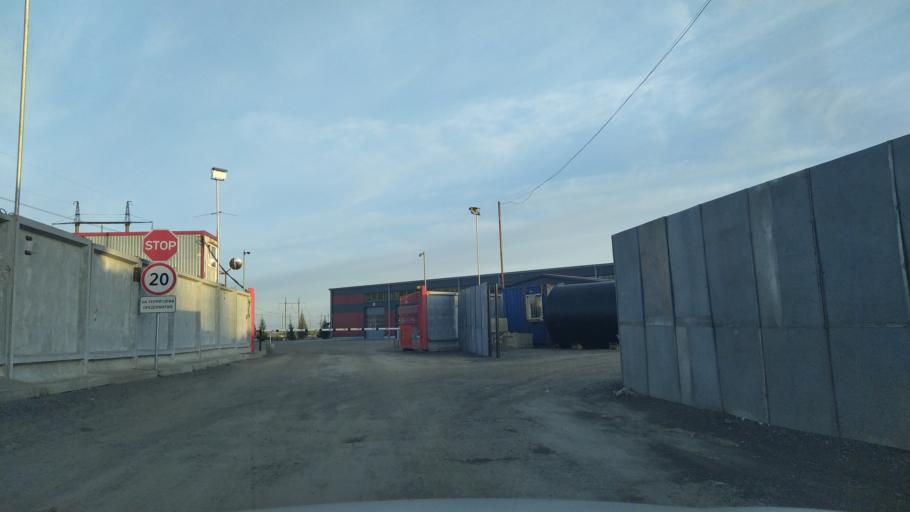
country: RU
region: St.-Petersburg
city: Obukhovo
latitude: 59.8027
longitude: 30.4602
